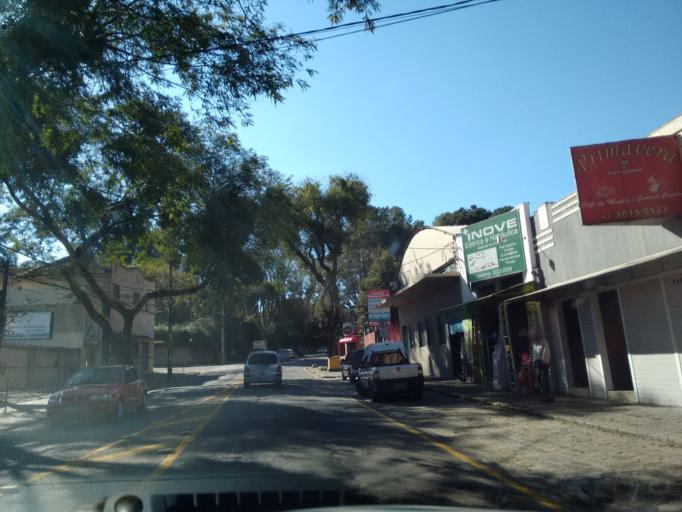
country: BR
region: Parana
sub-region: Curitiba
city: Curitiba
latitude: -25.3982
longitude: -49.2714
